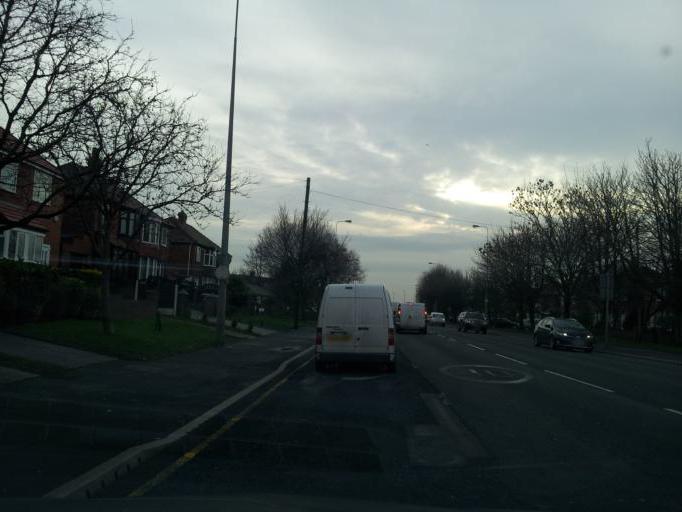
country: GB
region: England
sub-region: Borough of Oldham
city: Oldham
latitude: 53.5364
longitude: -2.1516
